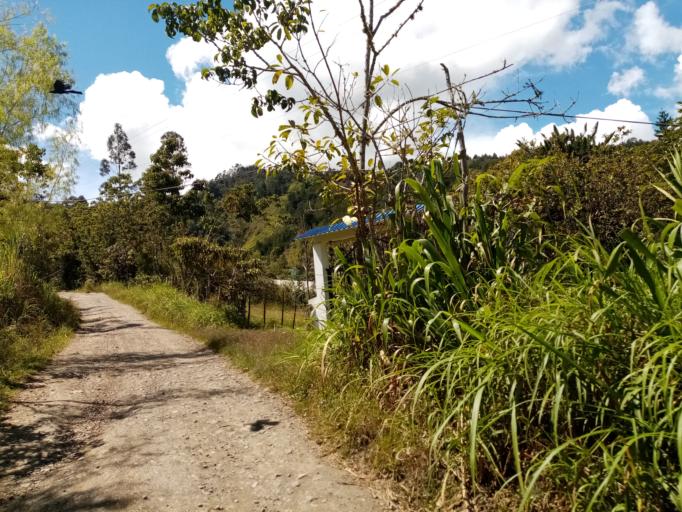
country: CO
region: Cundinamarca
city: Tenza
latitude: 5.0705
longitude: -73.4288
